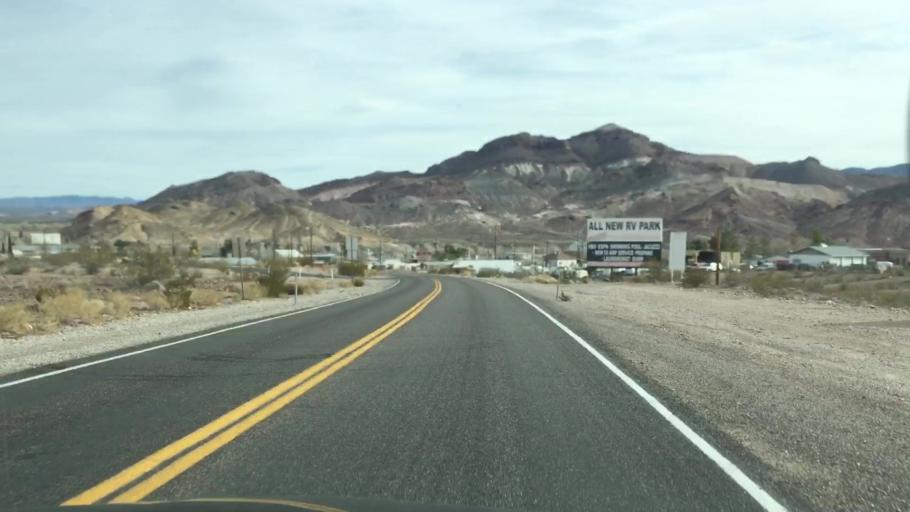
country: US
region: Nevada
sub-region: Nye County
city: Beatty
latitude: 36.9045
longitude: -116.7654
